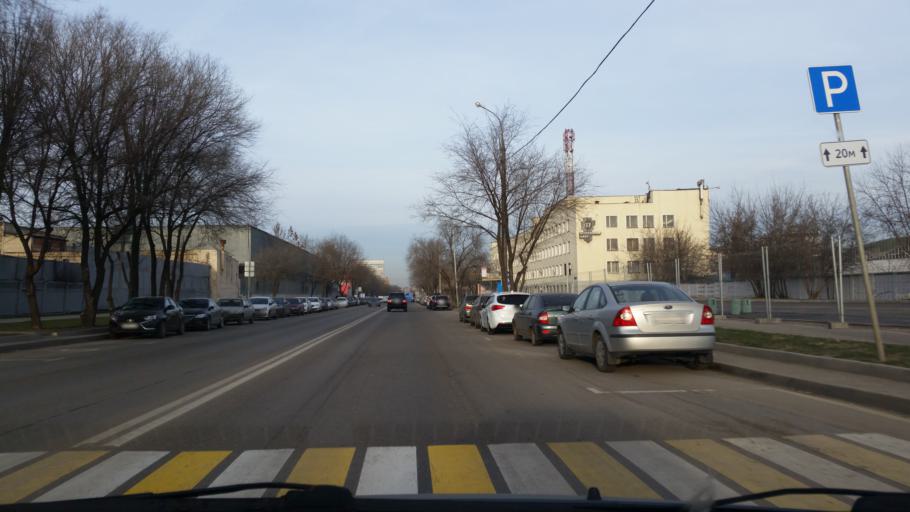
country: RU
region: Moscow
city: Chertanovo Yuzhnoye
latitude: 55.6102
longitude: 37.6169
